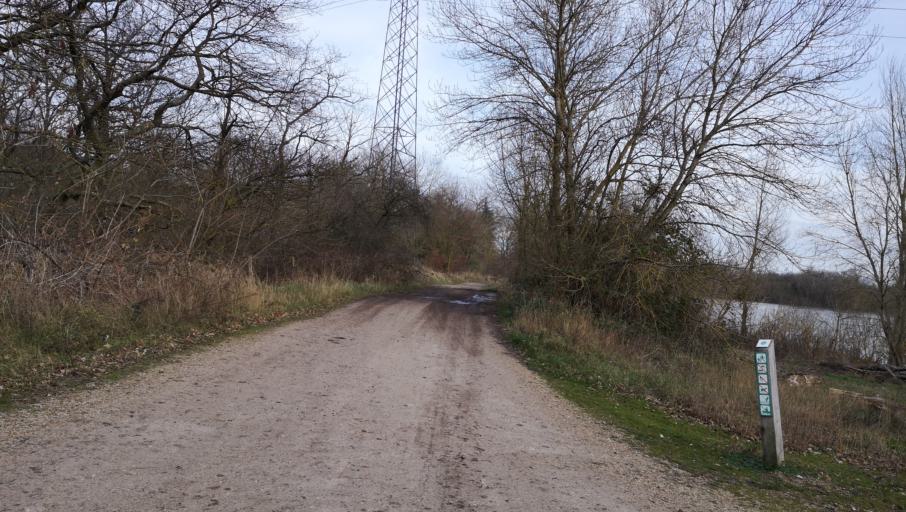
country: FR
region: Centre
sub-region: Departement du Loiret
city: Mareau-aux-Pres
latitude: 47.8664
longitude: 1.7970
